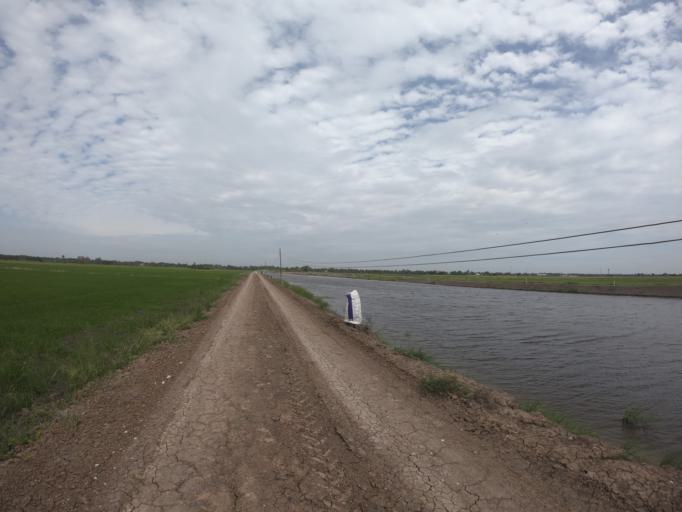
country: TH
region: Pathum Thani
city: Ban Lam Luk Ka
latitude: 14.0246
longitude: 100.8550
